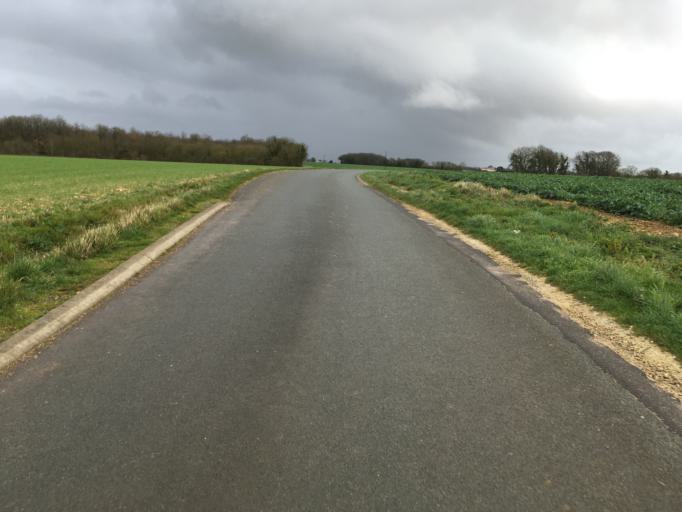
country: FR
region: Poitou-Charentes
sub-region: Departement de la Charente-Maritime
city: Surgeres
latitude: 46.1332
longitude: -0.7696
